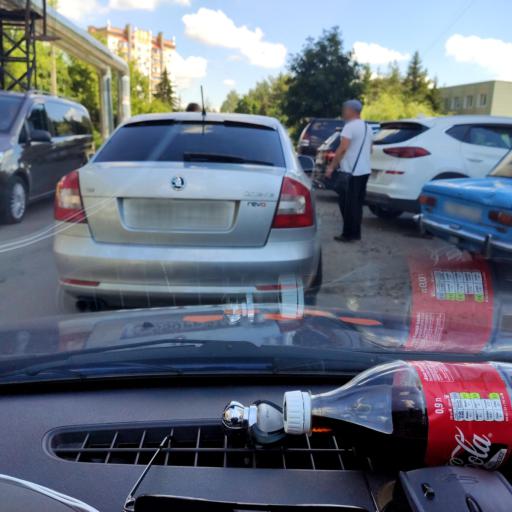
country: RU
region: Orjol
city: Orel
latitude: 52.9771
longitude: 36.0473
